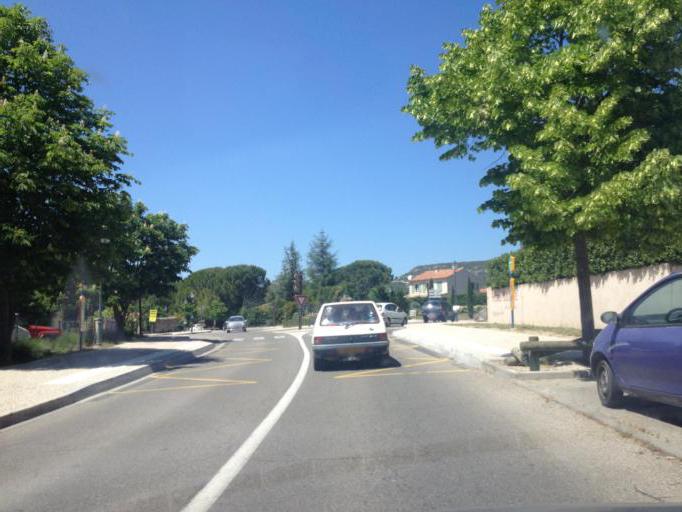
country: FR
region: Provence-Alpes-Cote d'Azur
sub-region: Departement du Vaucluse
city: Lourmarin
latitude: 43.7646
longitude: 5.3658
